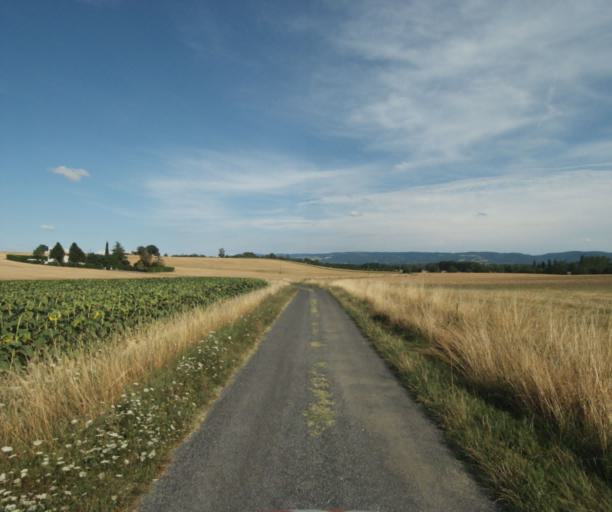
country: FR
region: Midi-Pyrenees
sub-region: Departement du Tarn
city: Puylaurens
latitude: 43.5299
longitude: 1.9959
